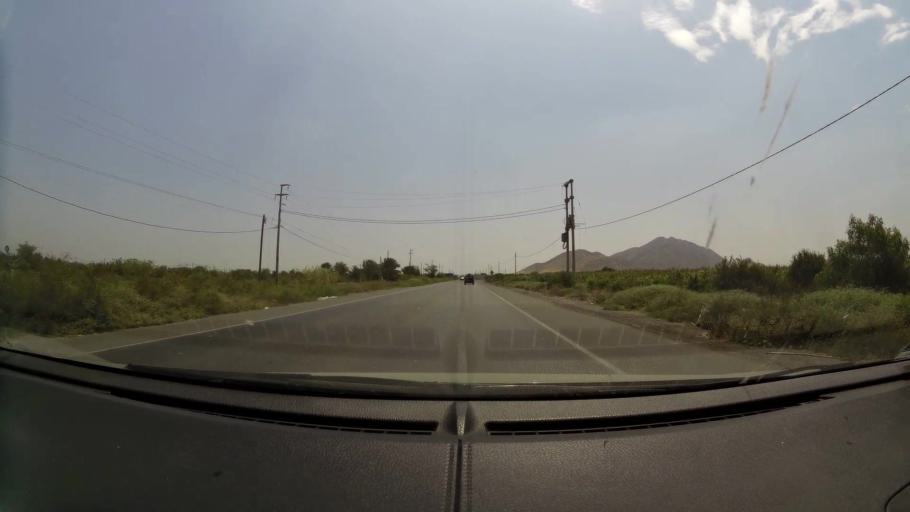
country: PE
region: La Libertad
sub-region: Chepen
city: Pacanga
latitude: -7.1205
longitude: -79.4859
